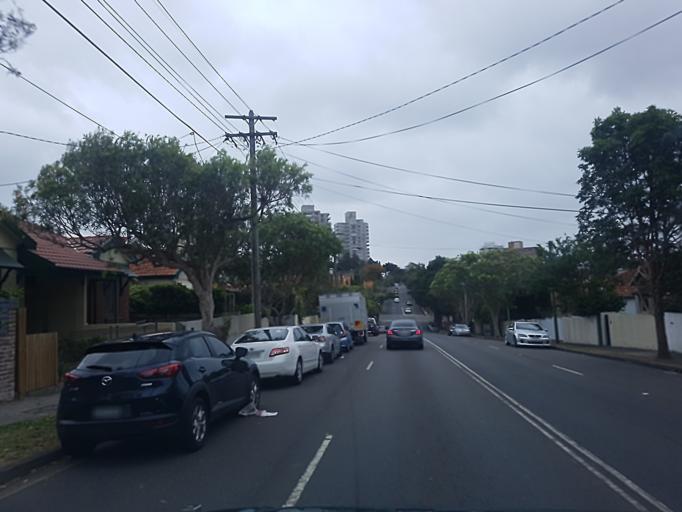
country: AU
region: New South Wales
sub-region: North Sydney
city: Cremorne
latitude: -33.8293
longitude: 151.2235
